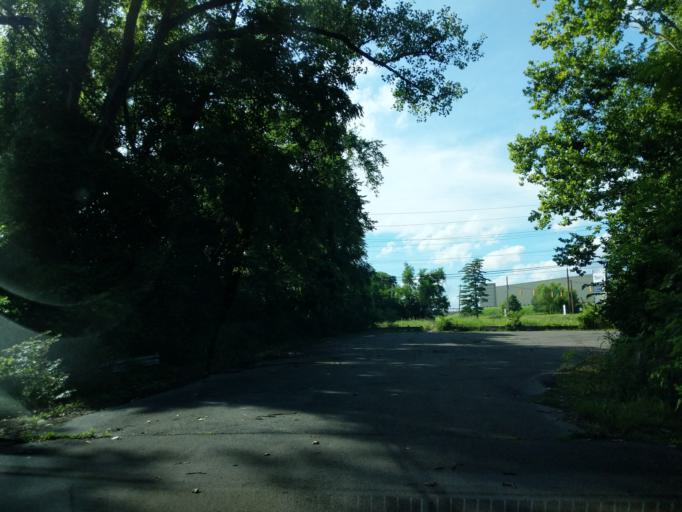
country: US
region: Tennessee
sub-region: Davidson County
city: Lakewood
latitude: 36.2655
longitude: -86.6559
